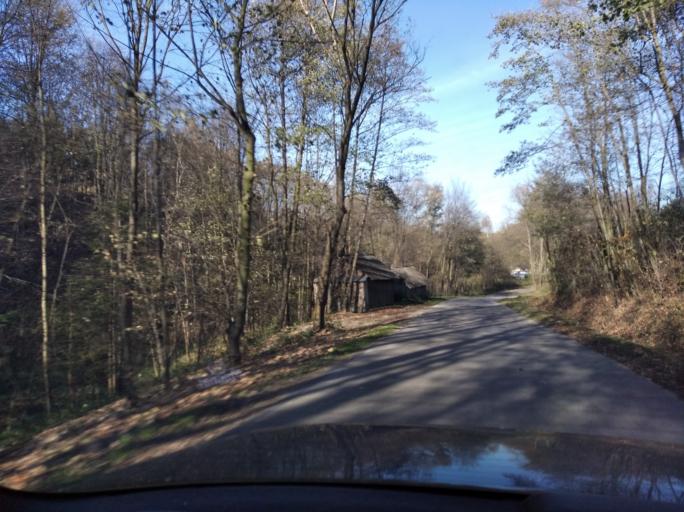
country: PL
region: Subcarpathian Voivodeship
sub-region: Powiat ropczycko-sedziszowski
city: Wielopole Skrzynskie
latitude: 49.9043
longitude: 21.5685
